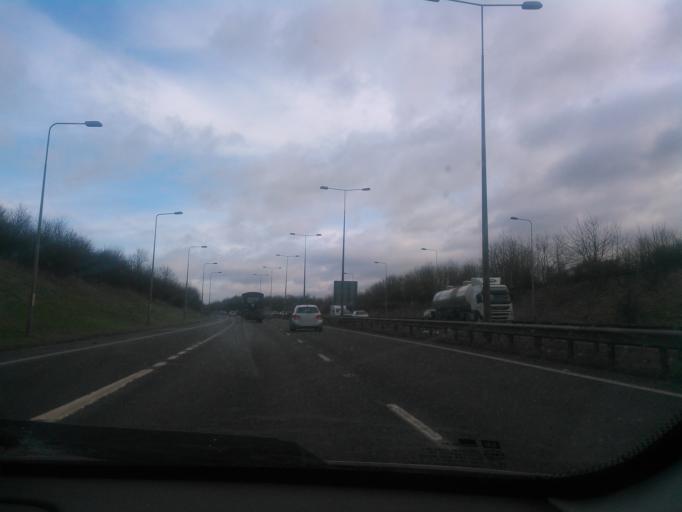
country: GB
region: England
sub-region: Derbyshire
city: Melbourne
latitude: 52.8602
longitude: -1.4332
